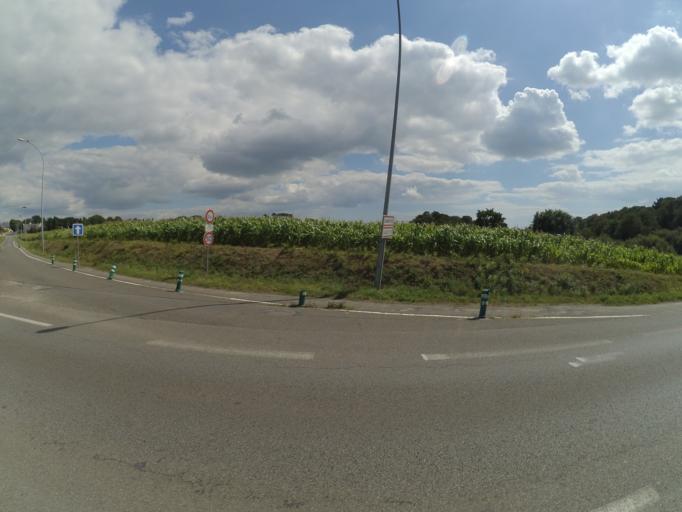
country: FR
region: Brittany
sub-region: Departement du Morbihan
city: Lanester
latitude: 47.7669
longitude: -3.3247
